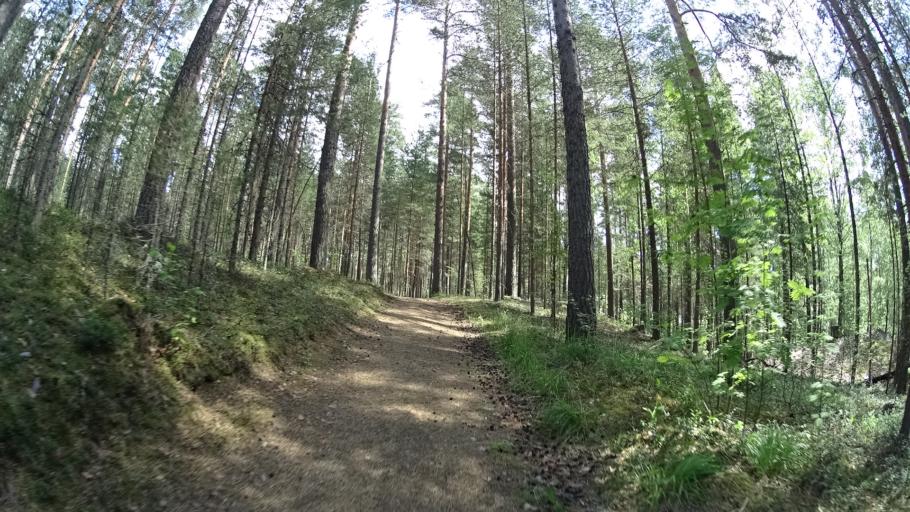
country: FI
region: Southern Savonia
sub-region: Savonlinna
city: Punkaharju
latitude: 61.7866
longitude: 29.3098
